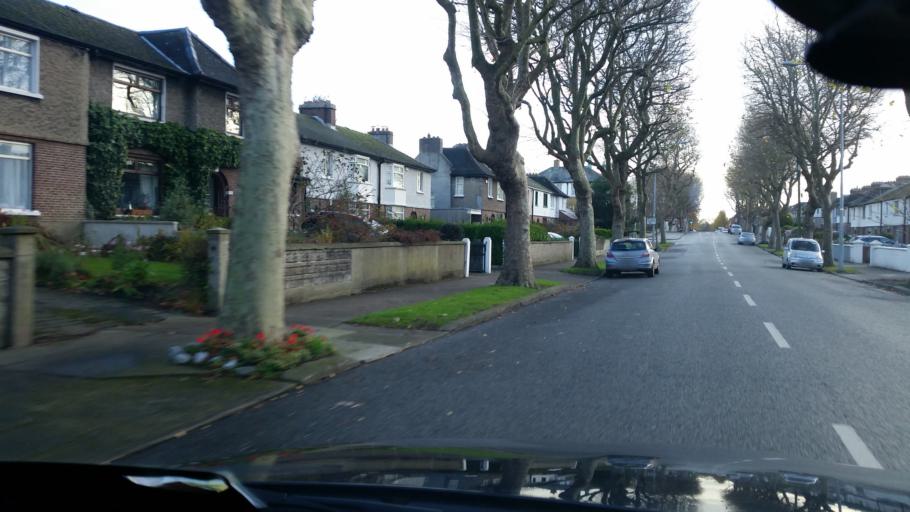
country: IE
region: Leinster
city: Glasnevin
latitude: 53.3751
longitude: -6.2597
